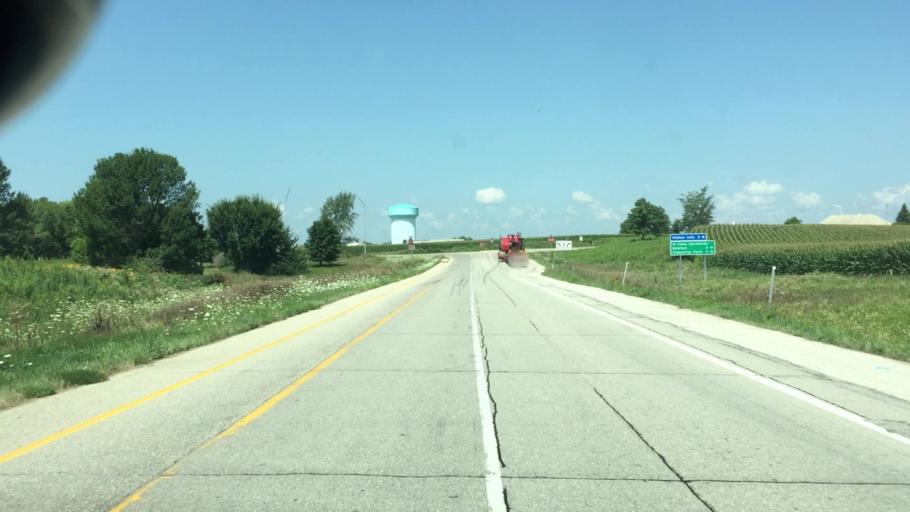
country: US
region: Iowa
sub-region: Jasper County
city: Newton
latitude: 41.6836
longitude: -92.9978
